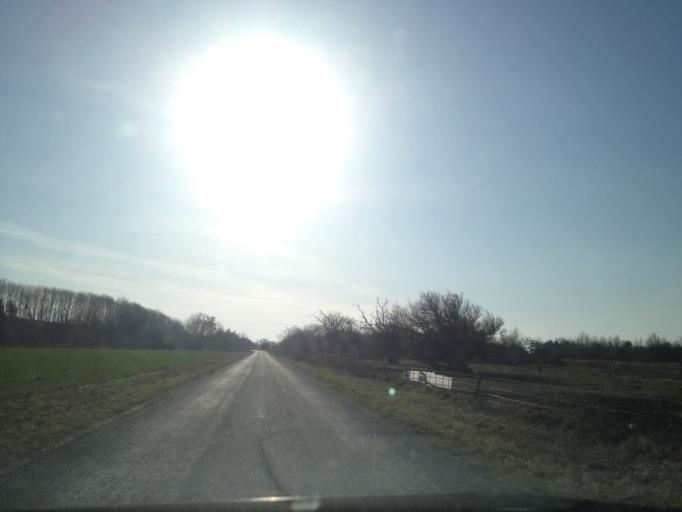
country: DK
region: South Denmark
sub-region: Kerteminde Kommune
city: Kerteminde
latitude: 55.5477
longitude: 10.6282
